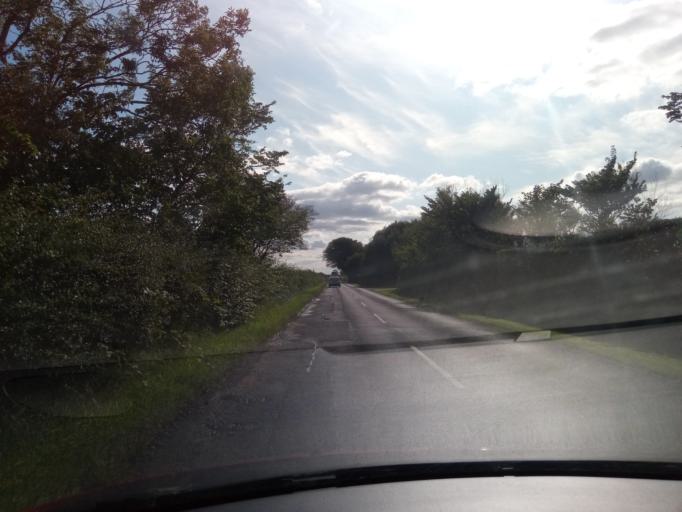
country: GB
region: Scotland
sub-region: The Scottish Borders
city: Allanton
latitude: 55.7503
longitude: -2.1555
